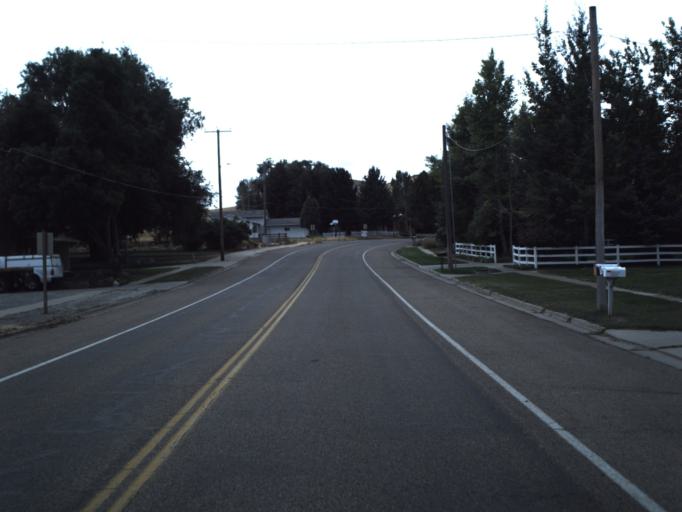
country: US
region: Utah
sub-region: Morgan County
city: Morgan
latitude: 41.0311
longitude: -111.6749
